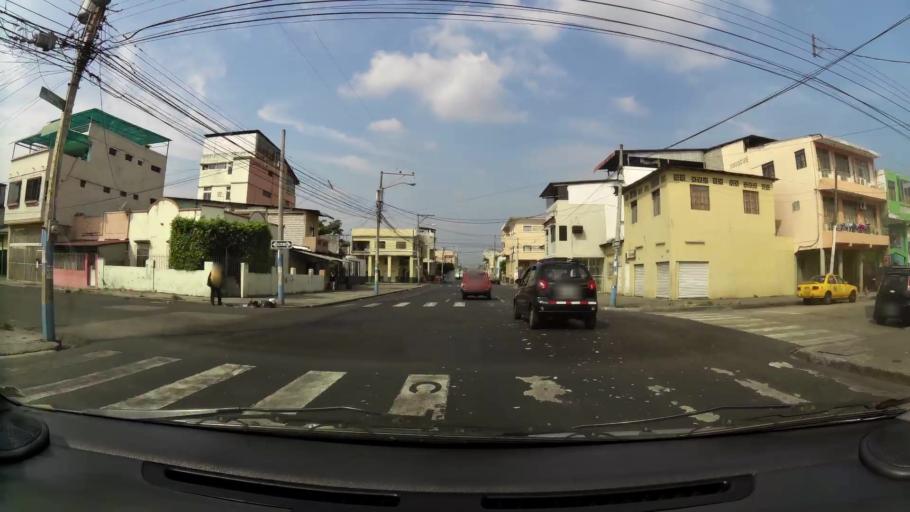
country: EC
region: Guayas
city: Guayaquil
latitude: -2.2020
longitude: -79.9010
